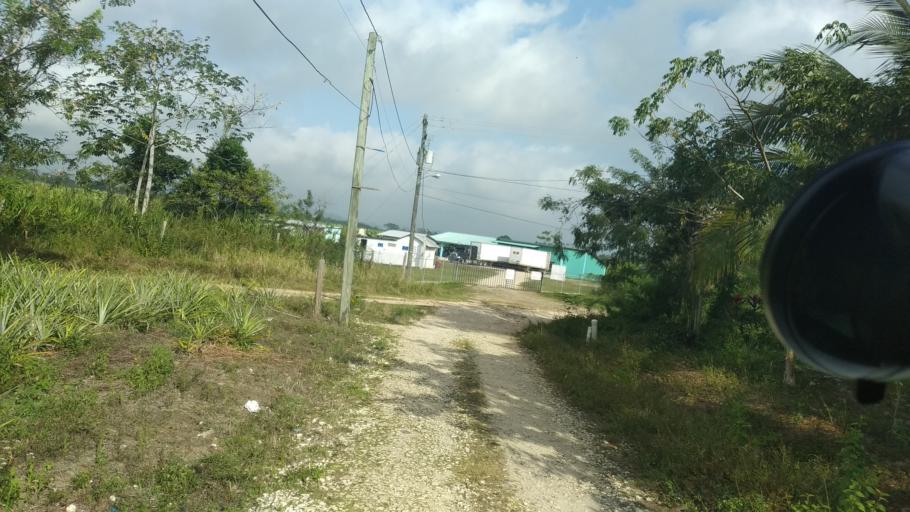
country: BZ
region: Stann Creek
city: Placencia
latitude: 16.5072
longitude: -88.5490
